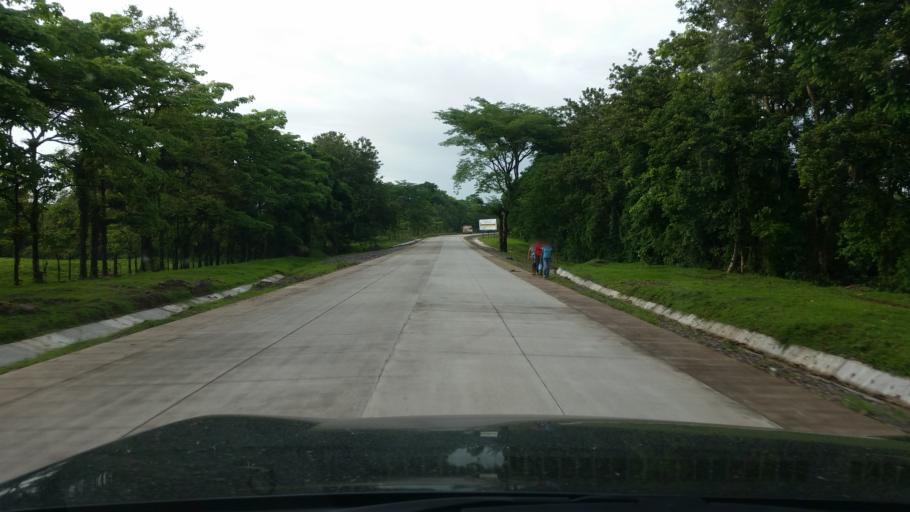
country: NI
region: Matagalpa
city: Rio Blanco
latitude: 13.1085
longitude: -85.0653
